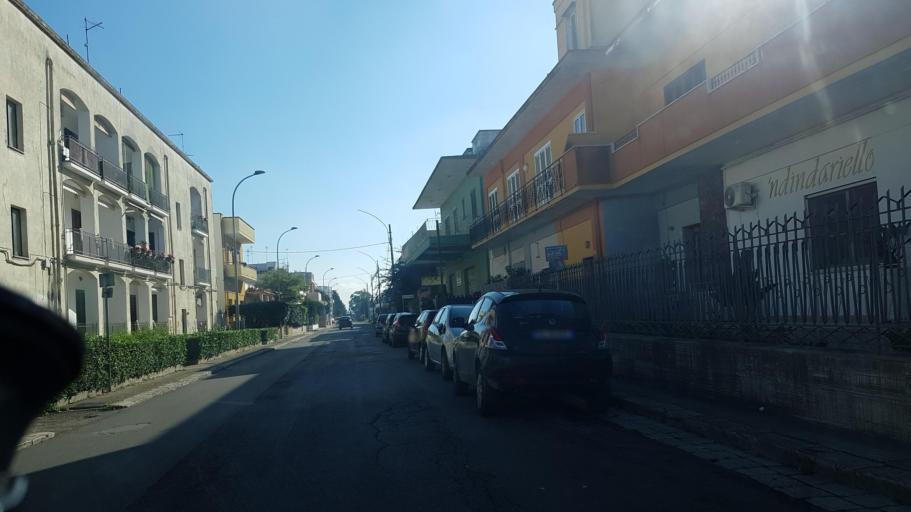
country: IT
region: Apulia
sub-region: Provincia di Lecce
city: Novoli
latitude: 40.3746
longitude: 18.0518
